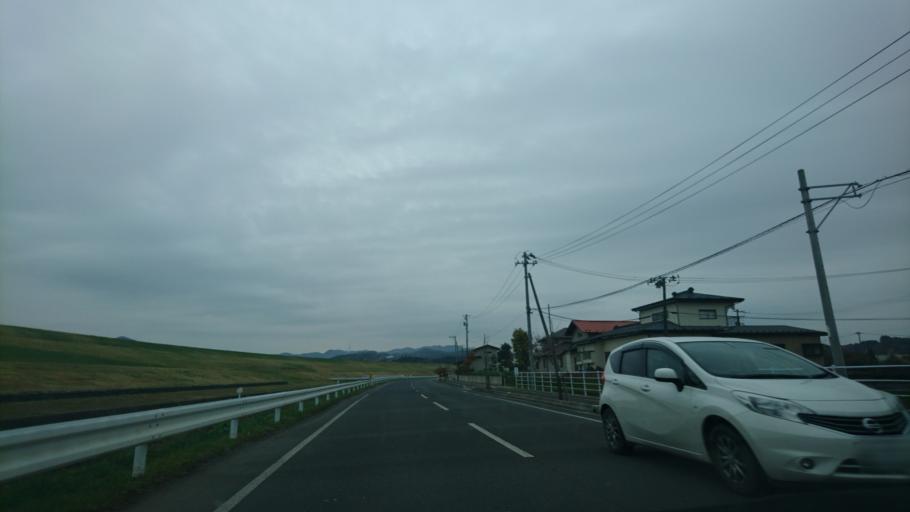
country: JP
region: Iwate
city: Ichinoseki
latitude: 38.9428
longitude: 141.1497
